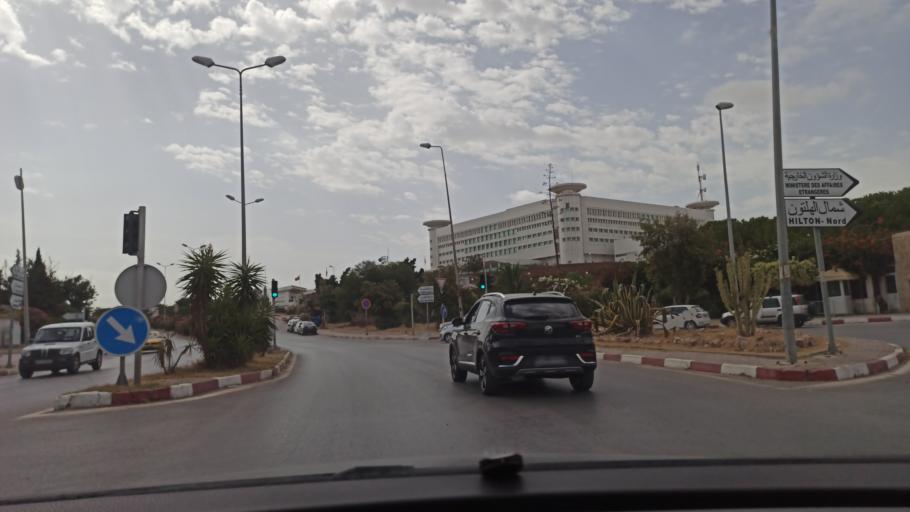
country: TN
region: Tunis
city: Tunis
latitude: 36.8309
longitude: 10.1577
